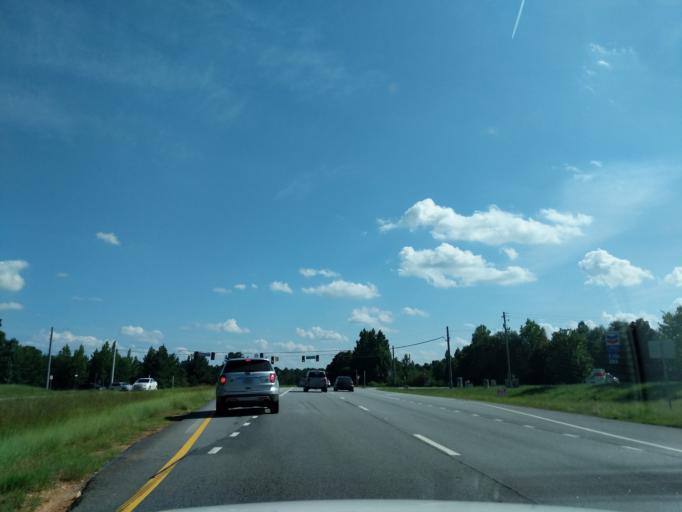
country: US
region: Georgia
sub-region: Jackson County
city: Commerce
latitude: 34.1946
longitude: -83.4319
